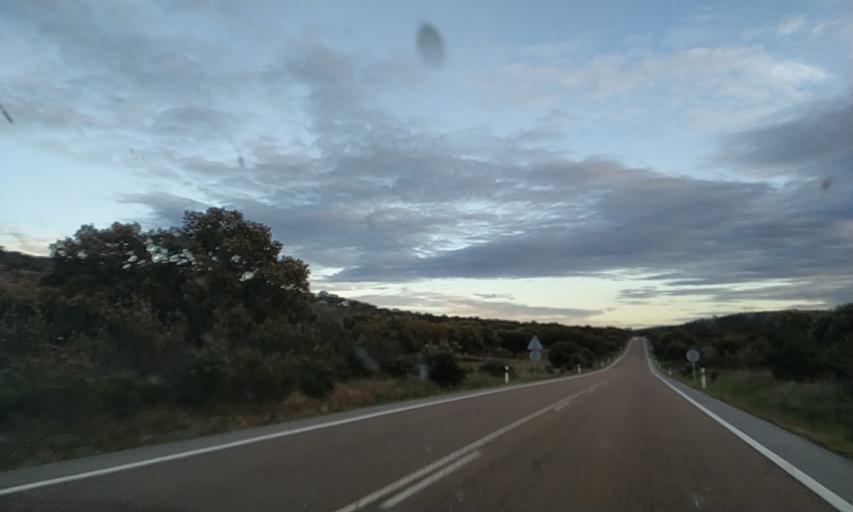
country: ES
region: Extremadura
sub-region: Provincia de Badajoz
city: Puebla de Obando
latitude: 39.2896
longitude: -6.5223
